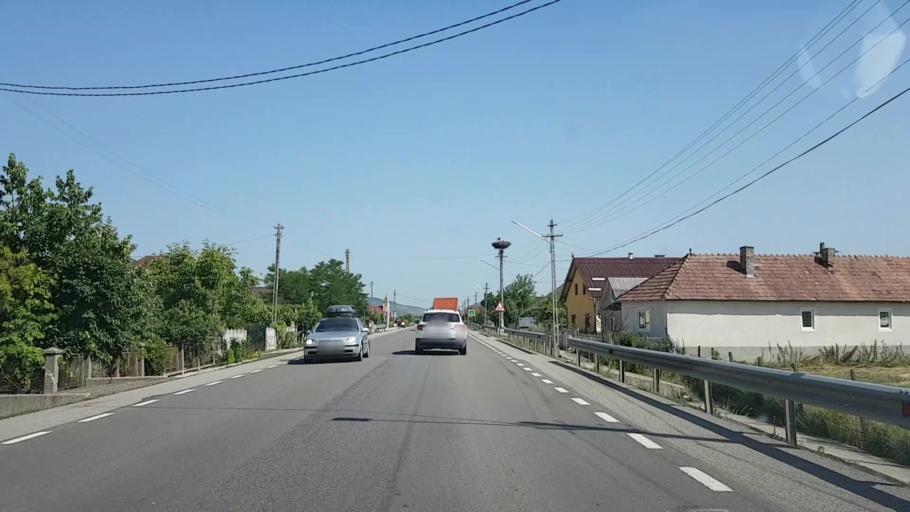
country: RO
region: Bistrita-Nasaud
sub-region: Comuna Sieu-Odorhei
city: Sieu-Odorhei
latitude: 47.1177
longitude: 24.3327
